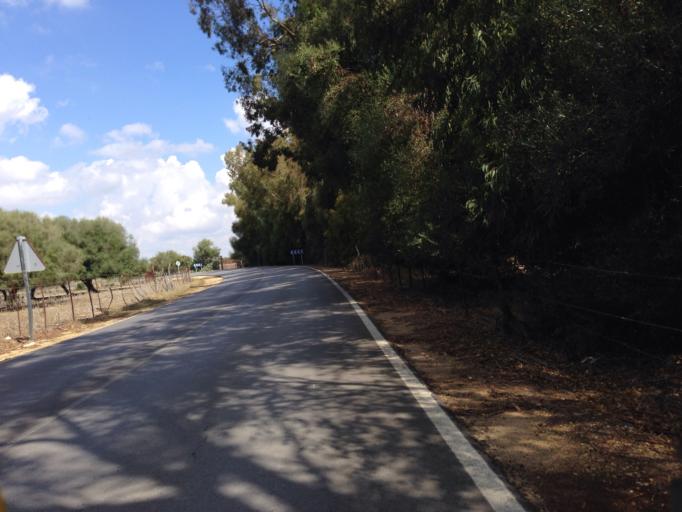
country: ES
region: Andalusia
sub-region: Provincia de Cadiz
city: Vejer de la Frontera
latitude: 36.2108
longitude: -6.0328
